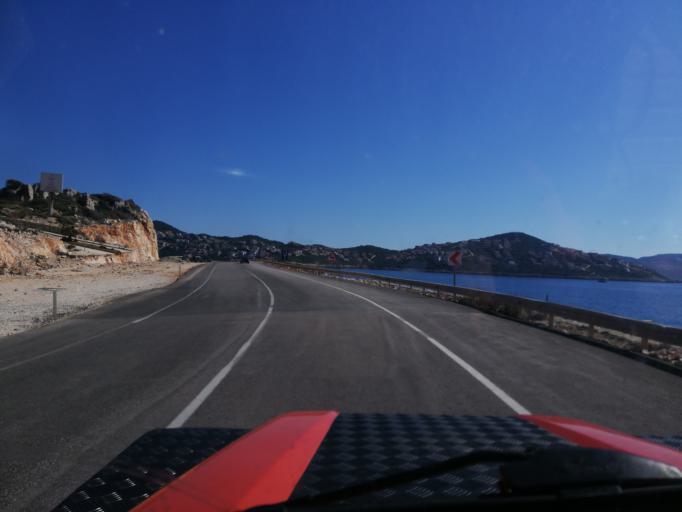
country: TR
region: Antalya
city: Kas
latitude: 36.2024
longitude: 29.5841
